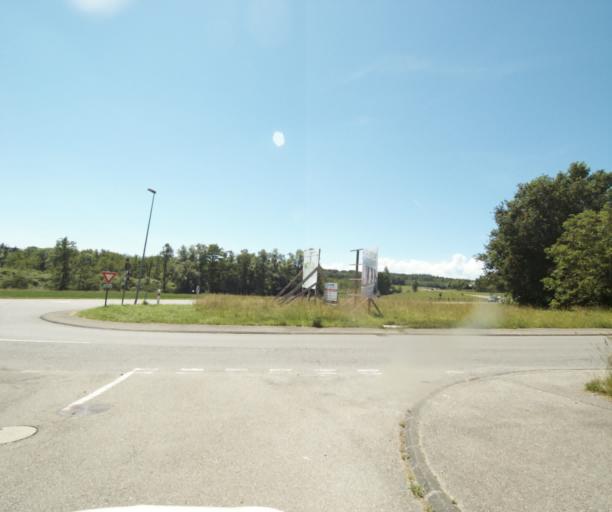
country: FR
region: Rhone-Alpes
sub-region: Departement de la Haute-Savoie
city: Bons-en-Chablais
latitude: 46.2726
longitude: 6.3520
